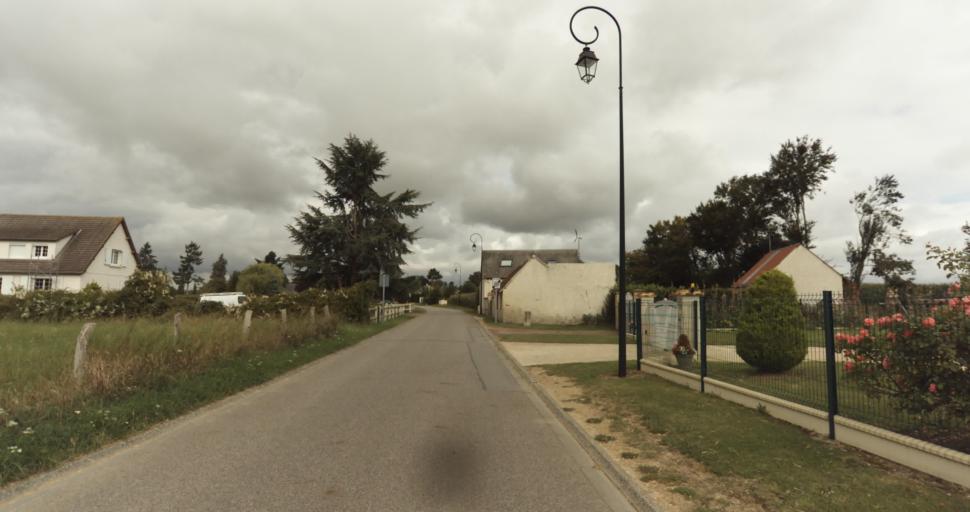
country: FR
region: Haute-Normandie
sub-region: Departement de l'Eure
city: Menilles
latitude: 48.9579
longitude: 1.2961
